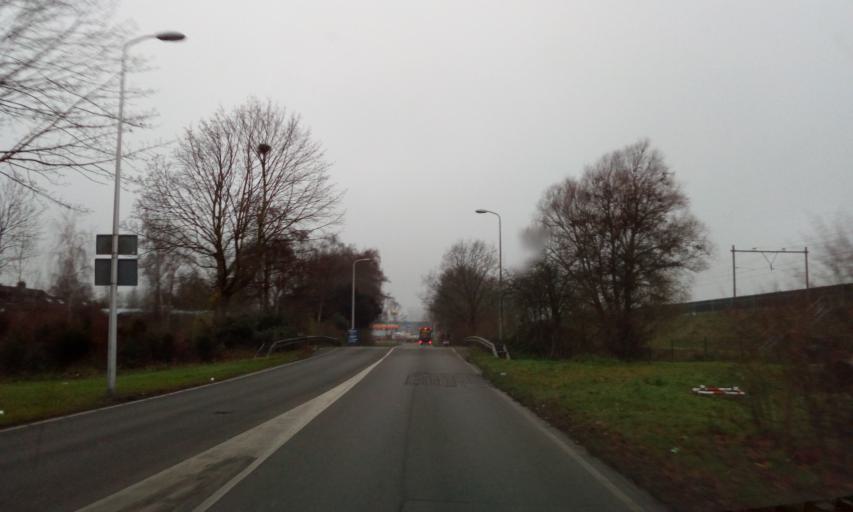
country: NL
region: South Holland
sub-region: Gemeente Capelle aan den IJssel
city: Capelle aan den IJssel
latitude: 51.9528
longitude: 4.5725
